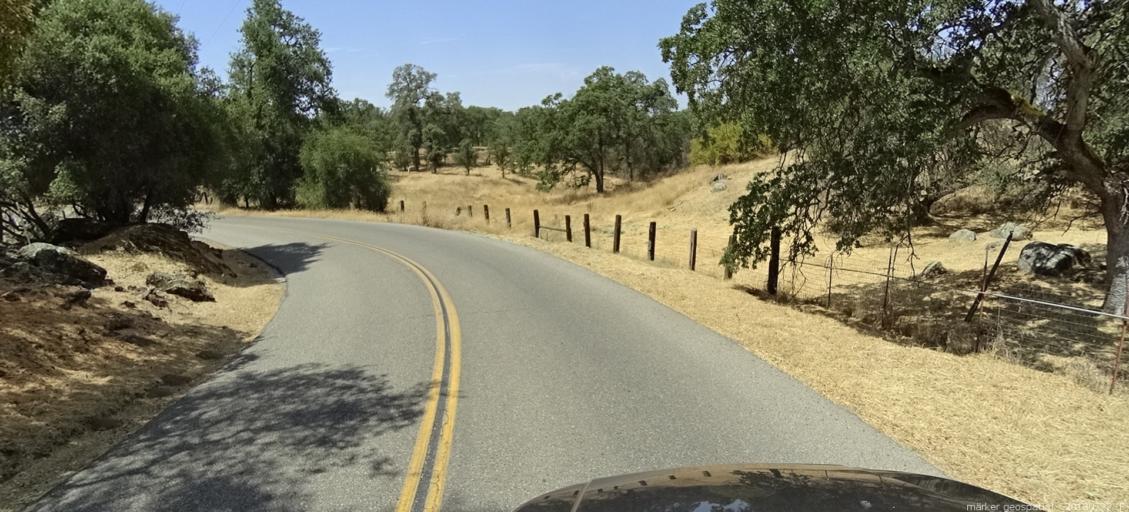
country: US
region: California
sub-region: Madera County
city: Coarsegold
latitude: 37.2767
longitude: -119.7432
